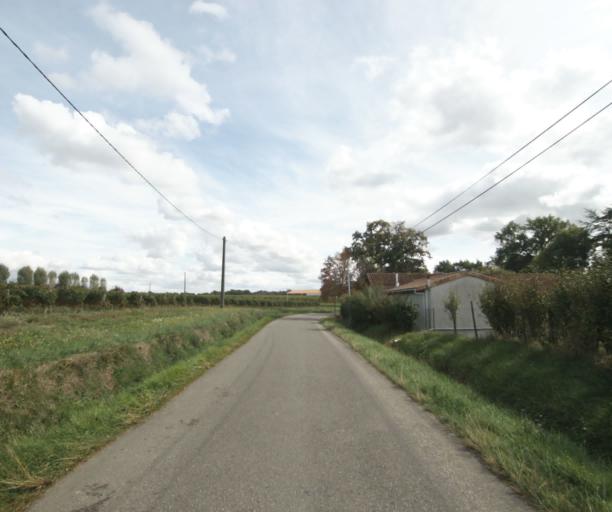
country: FR
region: Midi-Pyrenees
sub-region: Departement du Gers
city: Eauze
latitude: 43.8295
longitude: 0.1200
